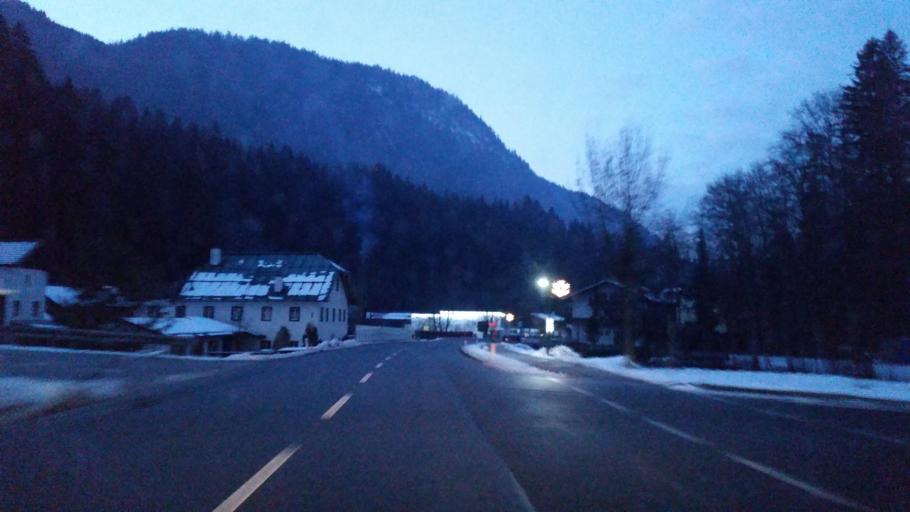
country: AT
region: Salzburg
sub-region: Politischer Bezirk Hallein
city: Abtenau
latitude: 47.5096
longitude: 13.4325
